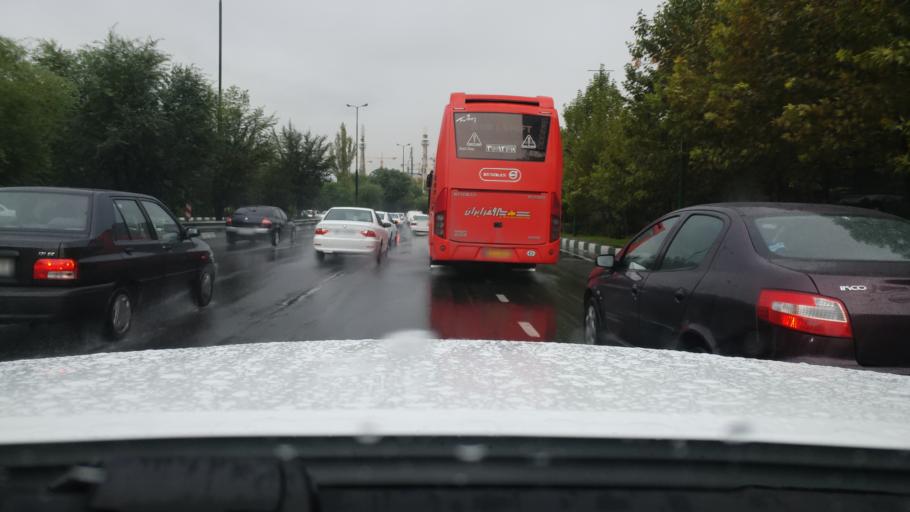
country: IR
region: Tehran
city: Tehran
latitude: 35.7449
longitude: 51.4212
